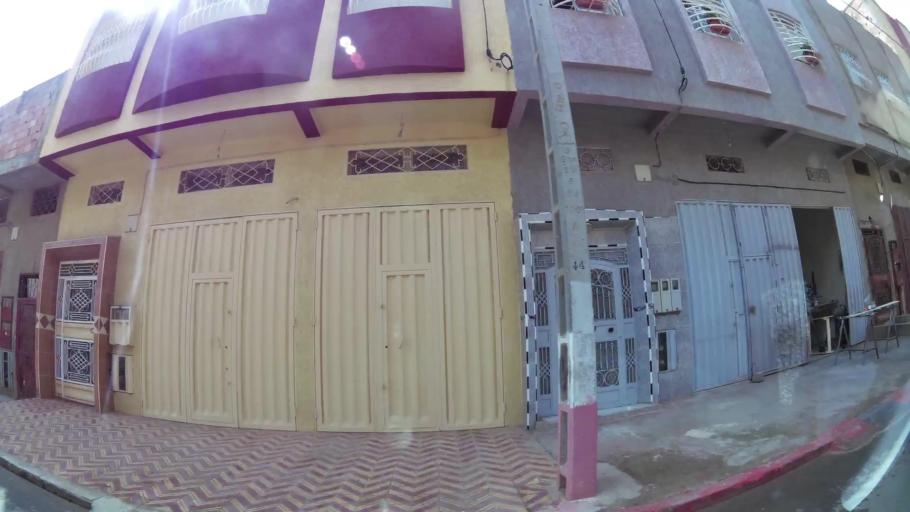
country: MA
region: Rabat-Sale-Zemmour-Zaer
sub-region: Khemisset
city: Tiflet
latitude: 33.8922
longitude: -6.3260
